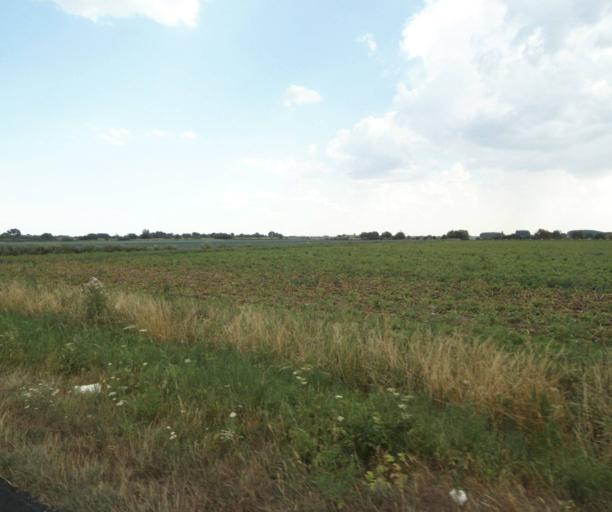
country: FR
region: Nord-Pas-de-Calais
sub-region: Departement du Nord
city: Deulemont
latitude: 50.7186
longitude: 2.9612
